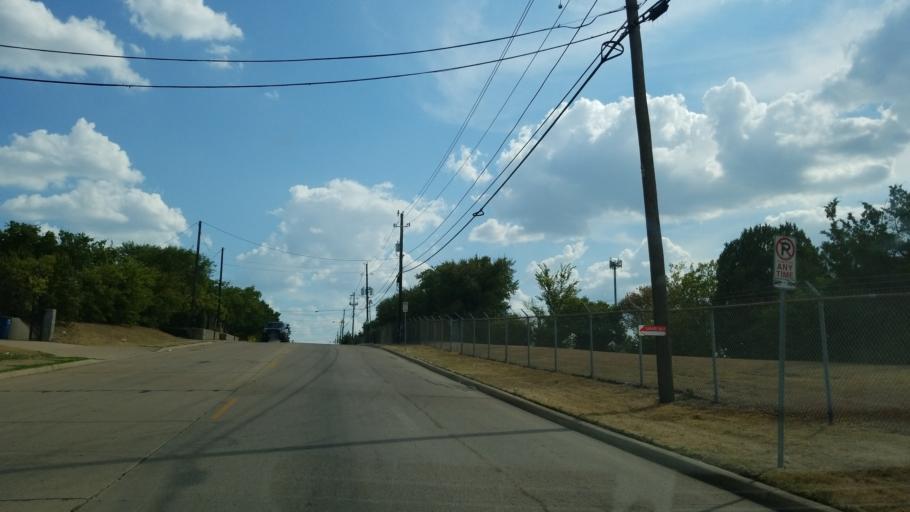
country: US
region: Texas
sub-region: Dallas County
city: Dallas
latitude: 32.7697
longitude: -96.8480
